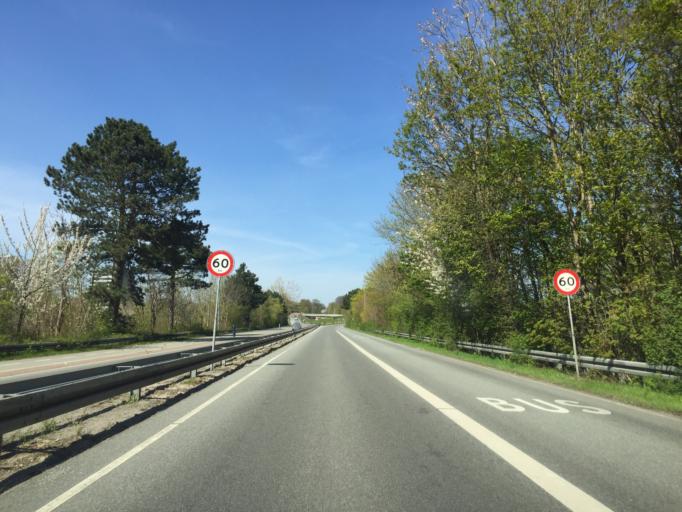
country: DK
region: Capital Region
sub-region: Gladsaxe Municipality
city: Buddinge
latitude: 55.7255
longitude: 12.4998
